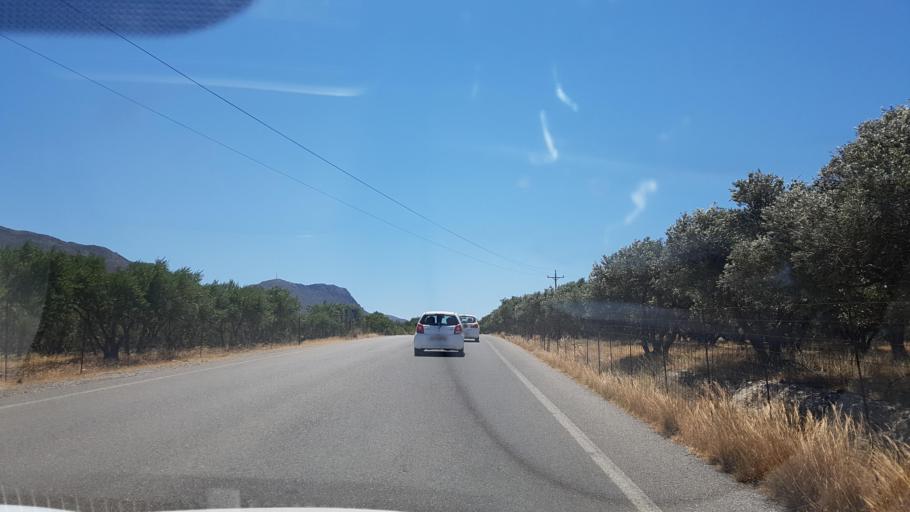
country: GR
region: Crete
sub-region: Nomos Chanias
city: Palaiochora
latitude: 35.2941
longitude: 23.5432
